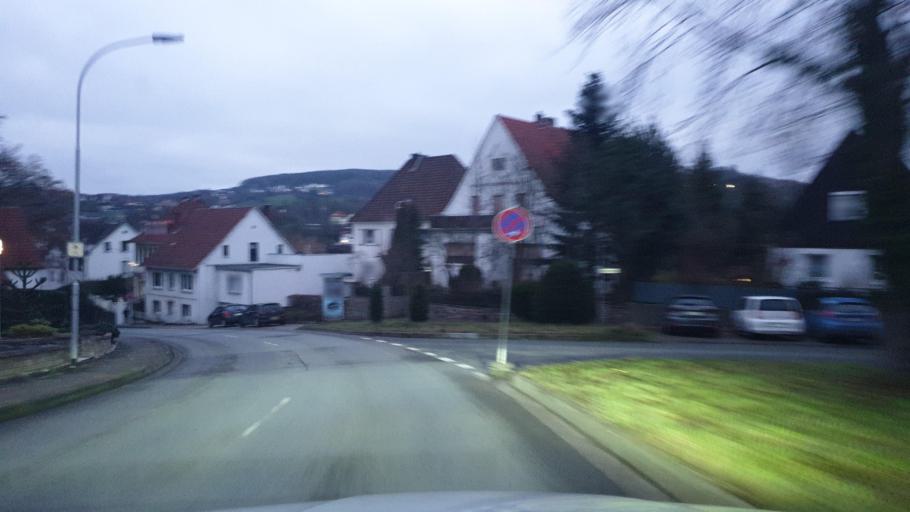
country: DE
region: North Rhine-Westphalia
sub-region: Regierungsbezirk Detmold
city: Vlotho
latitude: 52.1650
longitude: 8.8660
